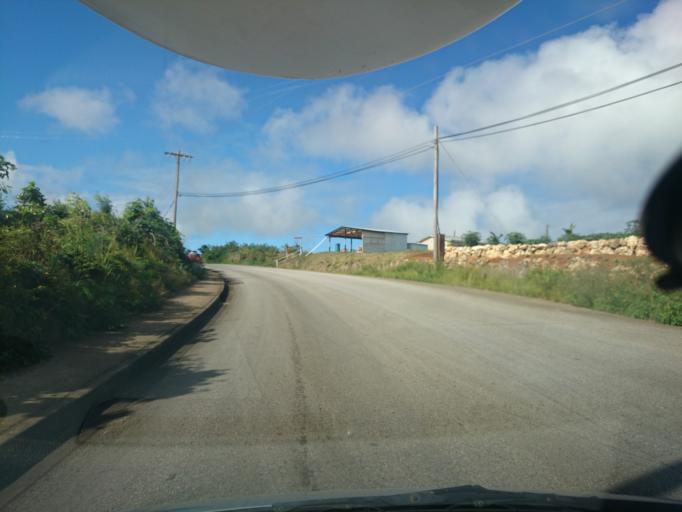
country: BB
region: Saint Thomas
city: Welchman Hall
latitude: 13.1889
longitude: -59.5442
